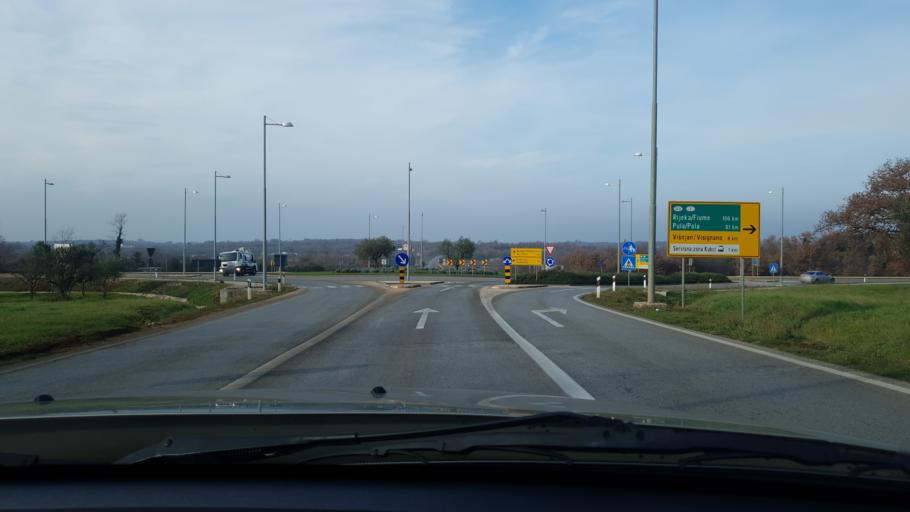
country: HR
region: Istarska
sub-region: Grad Porec
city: Porec
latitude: 45.2522
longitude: 13.6212
